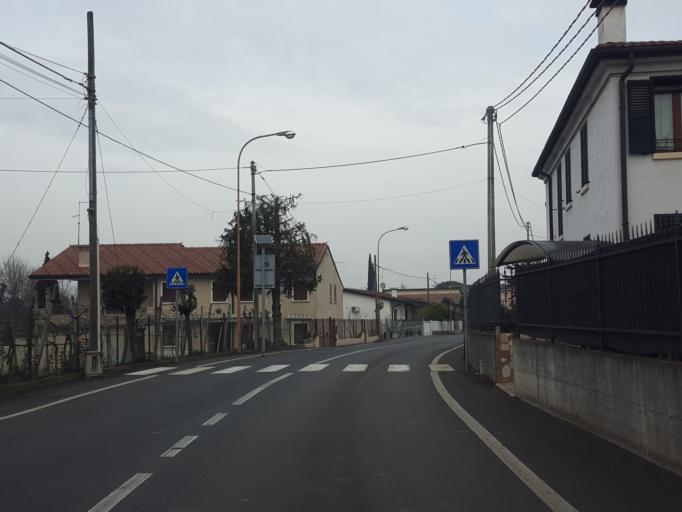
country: IT
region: Veneto
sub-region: Provincia di Verona
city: Arcole
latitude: 45.3627
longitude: 11.2847
